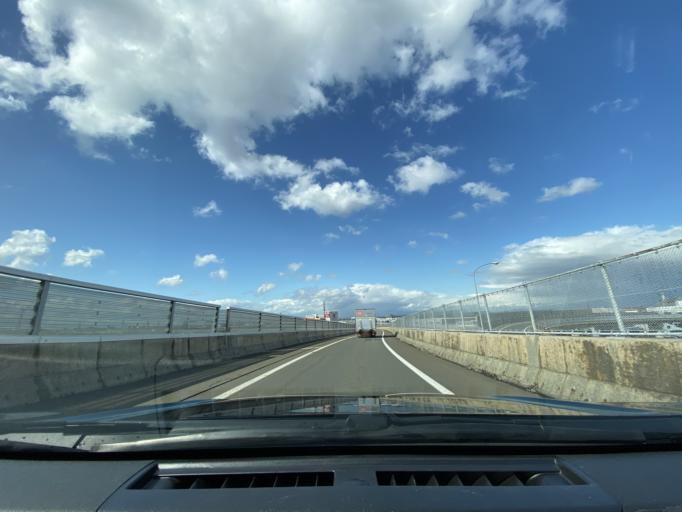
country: JP
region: Hokkaido
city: Sapporo
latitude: 43.0767
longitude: 141.4198
